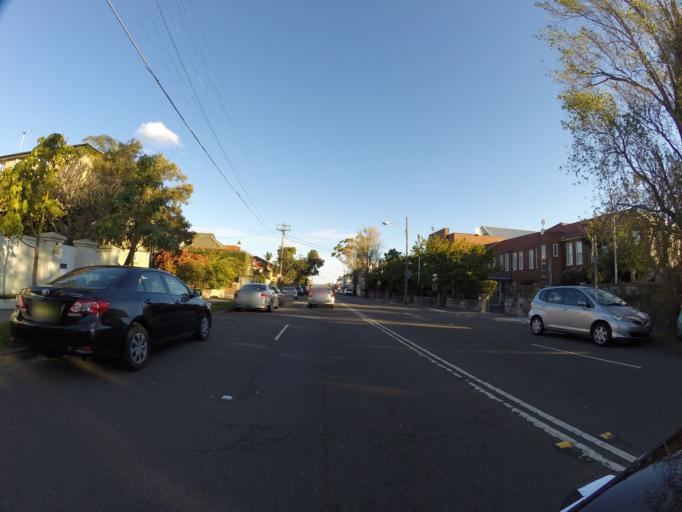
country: AU
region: New South Wales
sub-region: Waverley
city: Bondi Junction
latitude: -33.8988
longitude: 151.2539
